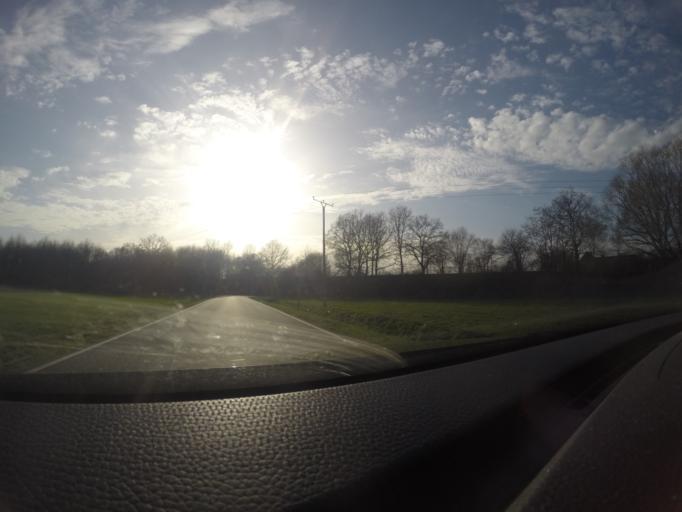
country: DE
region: North Rhine-Westphalia
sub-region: Regierungsbezirk Munster
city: Horstmar
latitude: 52.1002
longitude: 7.3326
